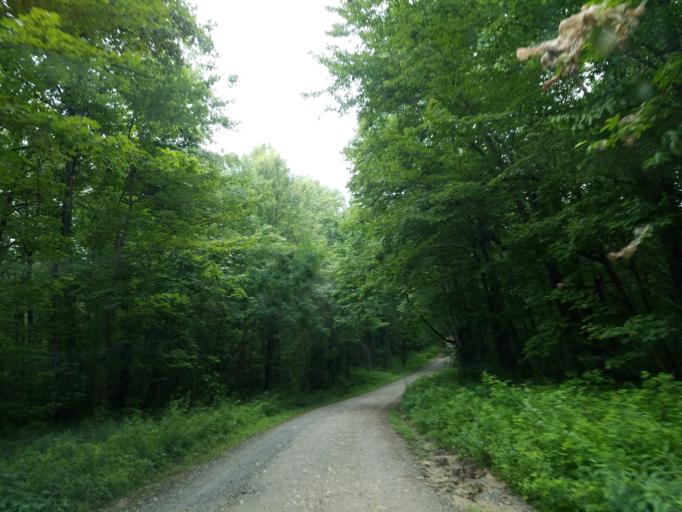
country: US
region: Georgia
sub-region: Lumpkin County
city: Dahlonega
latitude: 34.6404
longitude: -84.1611
